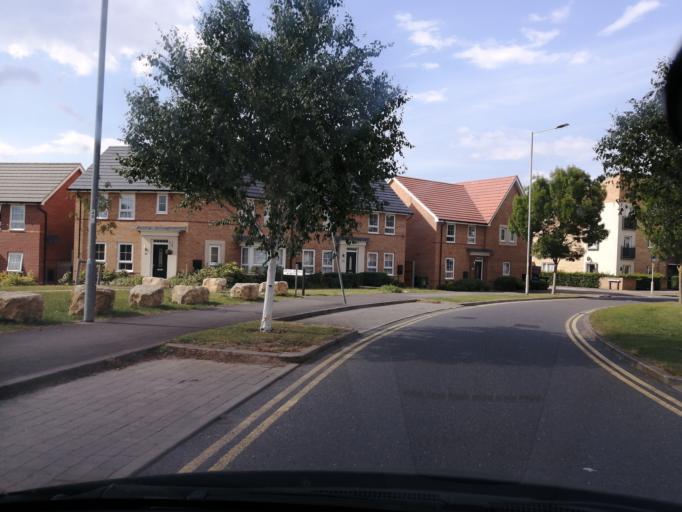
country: GB
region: England
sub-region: Peterborough
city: Peterborough
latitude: 52.5511
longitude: -0.2505
